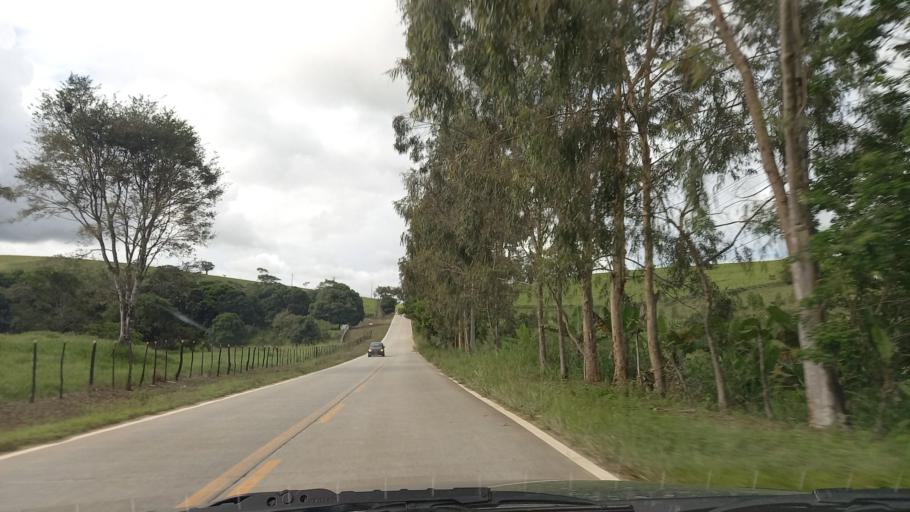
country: BR
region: Pernambuco
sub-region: Quipapa
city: Quipapa
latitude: -8.7791
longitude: -35.9337
